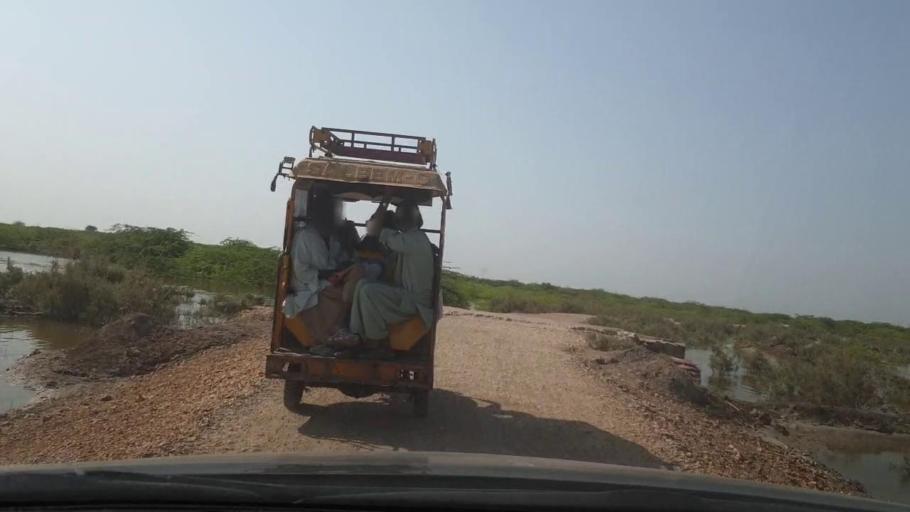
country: PK
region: Sindh
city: Naukot
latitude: 24.7961
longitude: 69.2196
